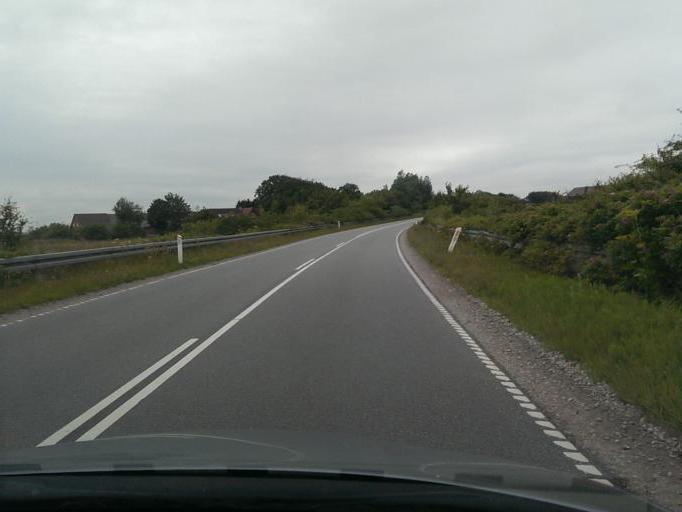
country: DK
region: North Denmark
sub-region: Hjorring Kommune
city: Vra
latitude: 57.3536
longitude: 9.9153
